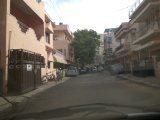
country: IN
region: Karnataka
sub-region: Bangalore Urban
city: Bangalore
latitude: 12.9810
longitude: 77.5382
